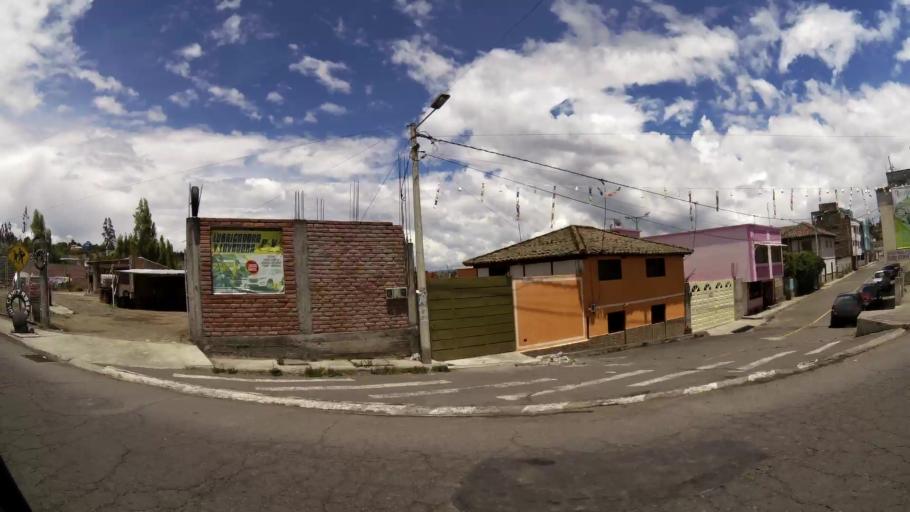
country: EC
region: Tungurahua
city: Pelileo
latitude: -1.3162
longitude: -78.5975
